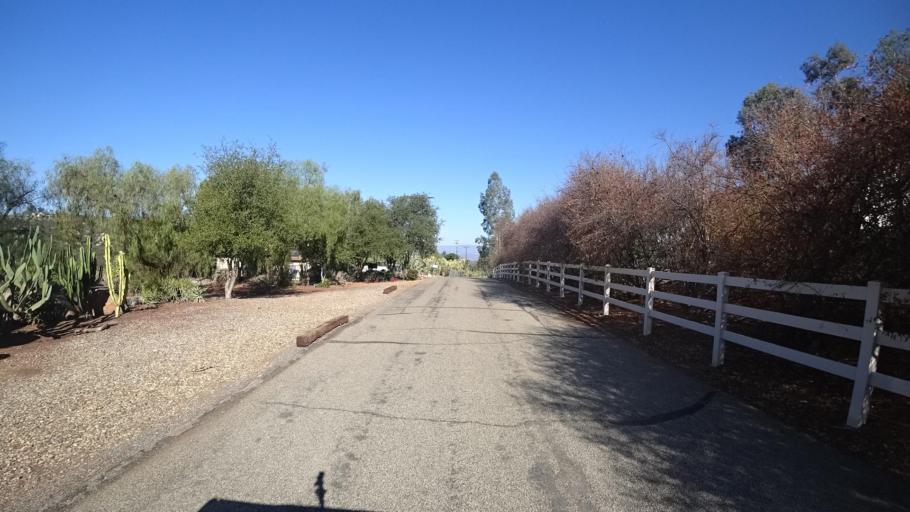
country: US
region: California
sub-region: San Diego County
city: Hidden Meadows
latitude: 33.2399
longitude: -117.1213
